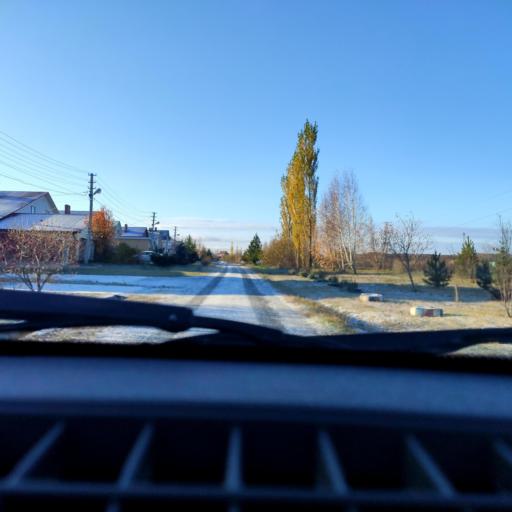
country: RU
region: Bashkortostan
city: Avdon
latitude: 54.6957
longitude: 55.7878
